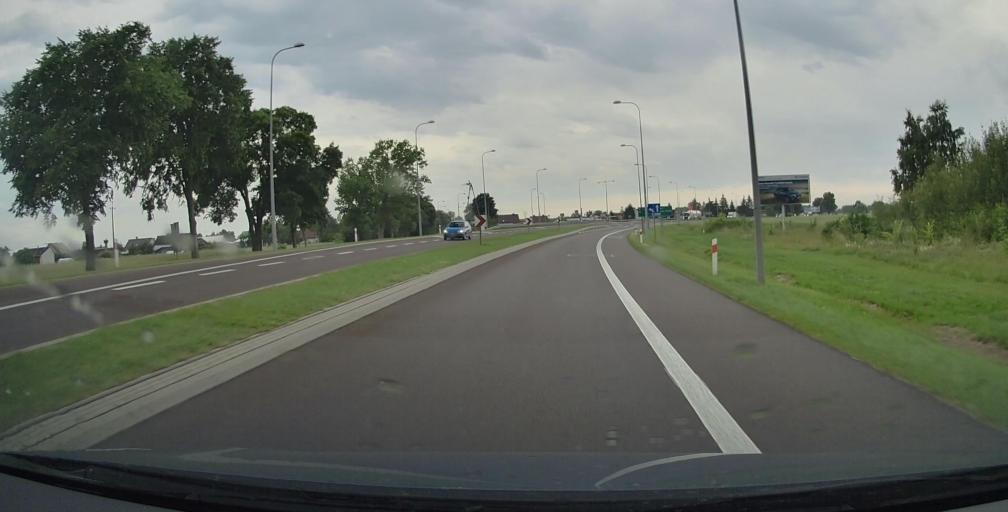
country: PL
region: Lublin Voivodeship
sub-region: Powiat bialski
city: Miedzyrzec Podlaski
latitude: 52.0004
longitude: 22.8162
